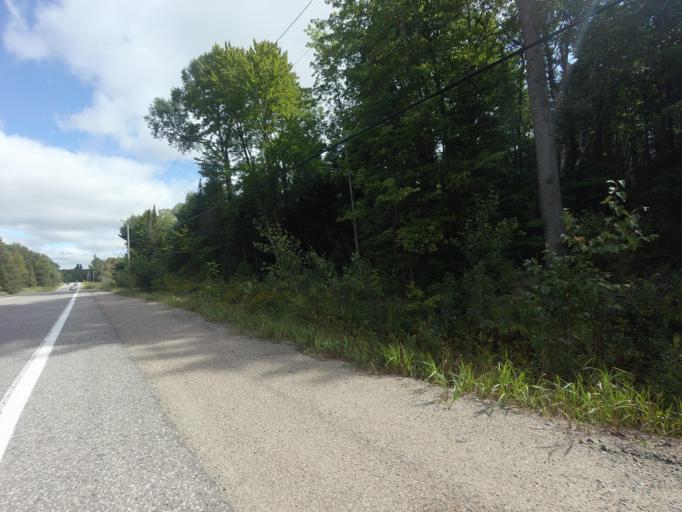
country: CA
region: Ontario
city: Omemee
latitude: 44.7939
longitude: -78.6394
